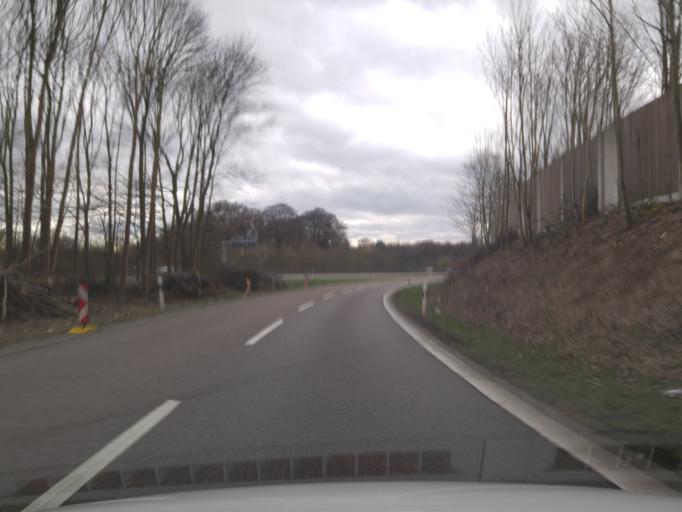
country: DE
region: North Rhine-Westphalia
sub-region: Regierungsbezirk Dusseldorf
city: Hilden
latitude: 51.1947
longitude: 6.9359
